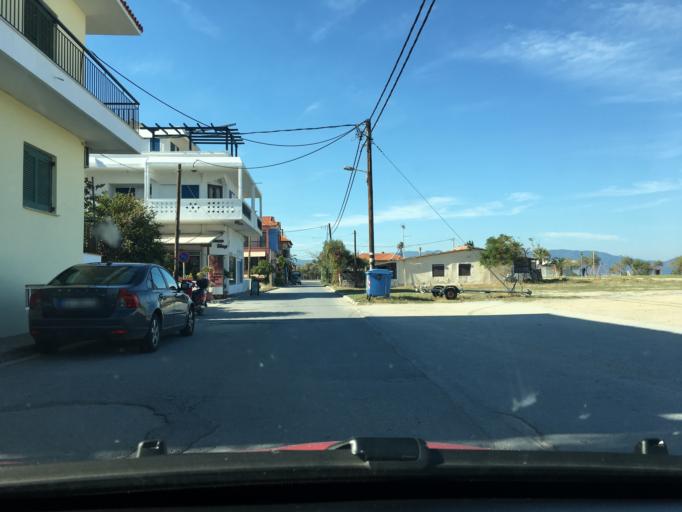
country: GR
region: Central Macedonia
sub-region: Nomos Chalkidikis
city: Ierissos
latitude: 40.4007
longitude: 23.8797
